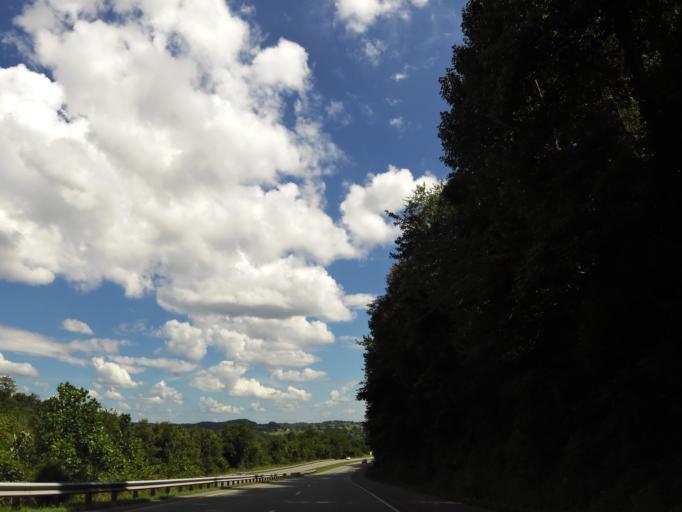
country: US
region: Tennessee
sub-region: Claiborne County
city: Harrogate
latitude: 36.5903
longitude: -83.6603
